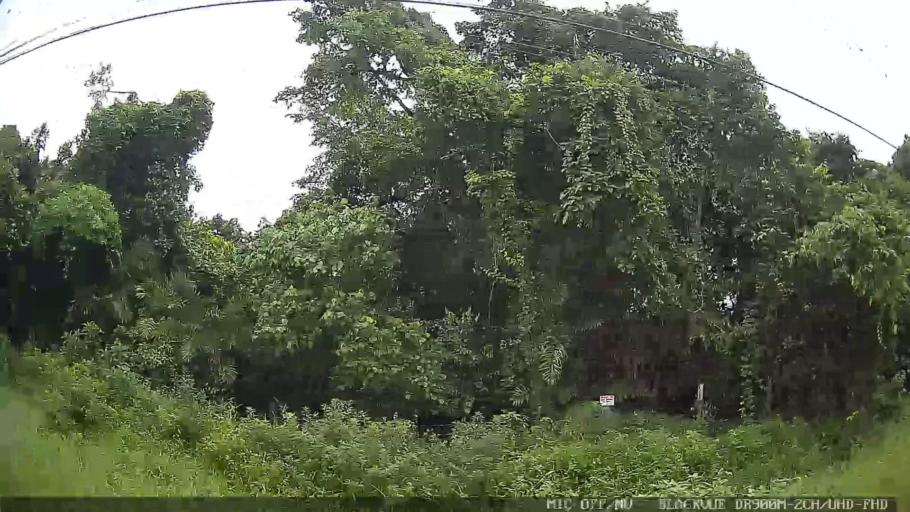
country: BR
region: Sao Paulo
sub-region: Sao Sebastiao
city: Sao Sebastiao
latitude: -23.7069
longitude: -45.4523
